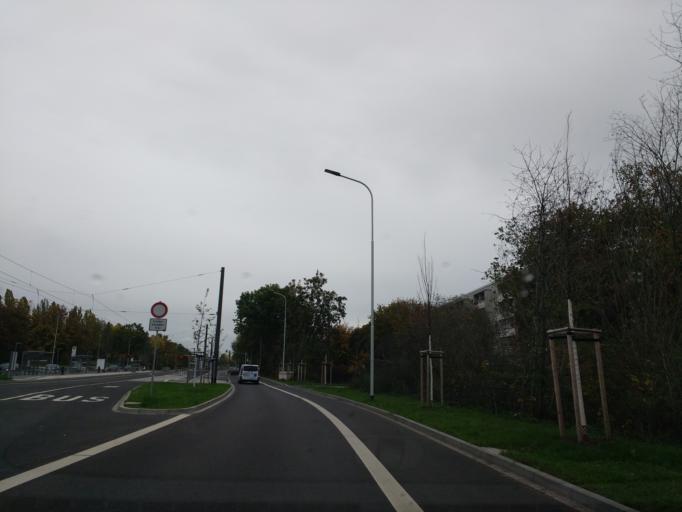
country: DE
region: Saxony-Anhalt
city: Halle Neustadt
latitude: 51.4875
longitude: 11.9454
